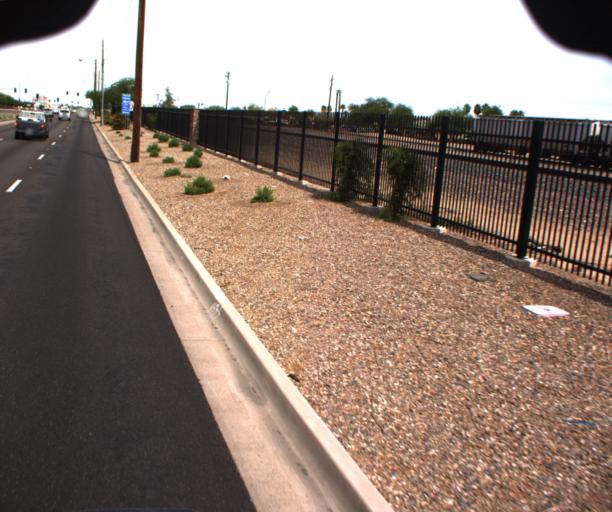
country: US
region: Arizona
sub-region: Maricopa County
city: Peoria
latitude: 33.5797
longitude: -112.2354
